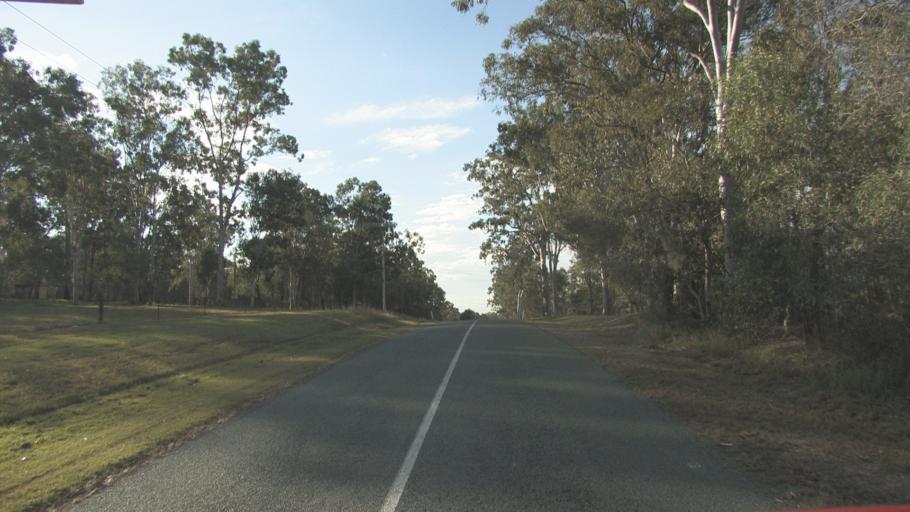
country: AU
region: Queensland
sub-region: Gold Coast
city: Ormeau Hills
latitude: -27.8352
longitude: 153.1692
